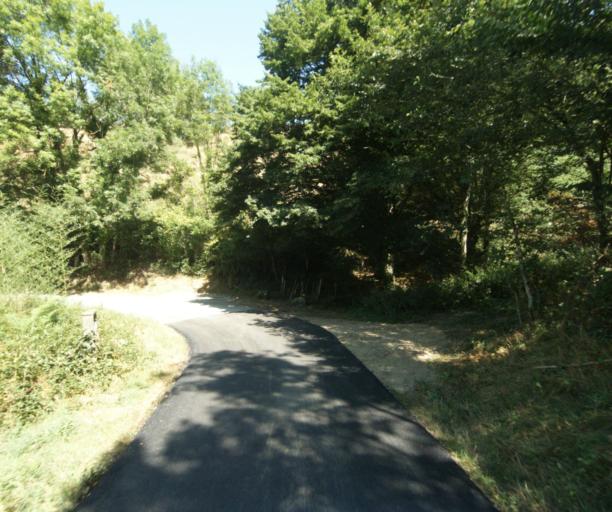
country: FR
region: Rhone-Alpes
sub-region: Departement du Rhone
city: Courzieu
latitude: 45.7244
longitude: 4.5266
